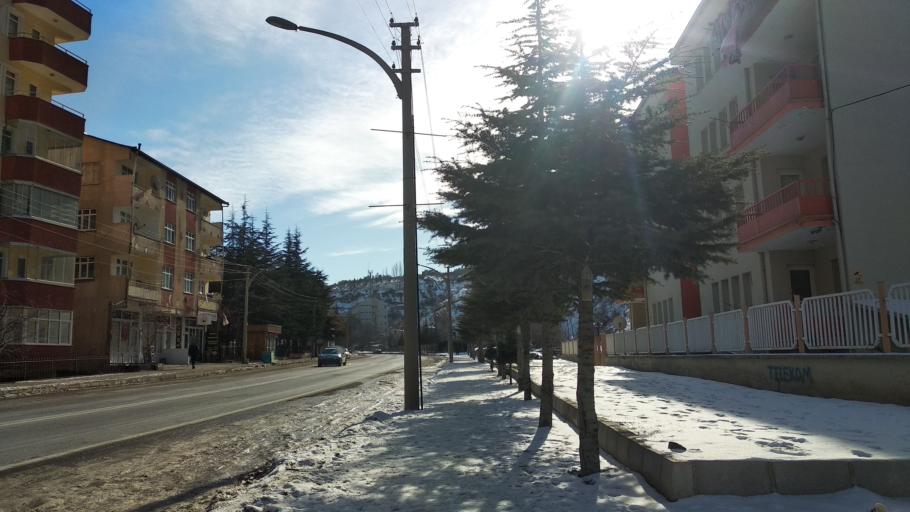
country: TR
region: Gumushane
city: Gumushkhane
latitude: 40.4491
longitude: 39.4962
